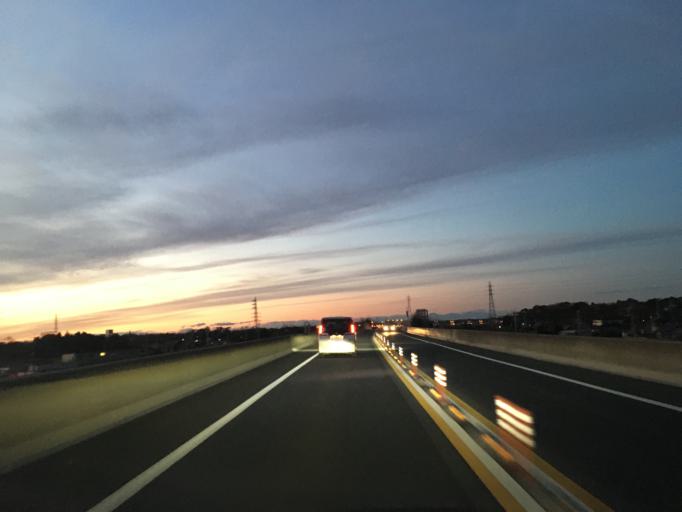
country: JP
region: Ibaraki
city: Naka
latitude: 36.0422
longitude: 140.1102
